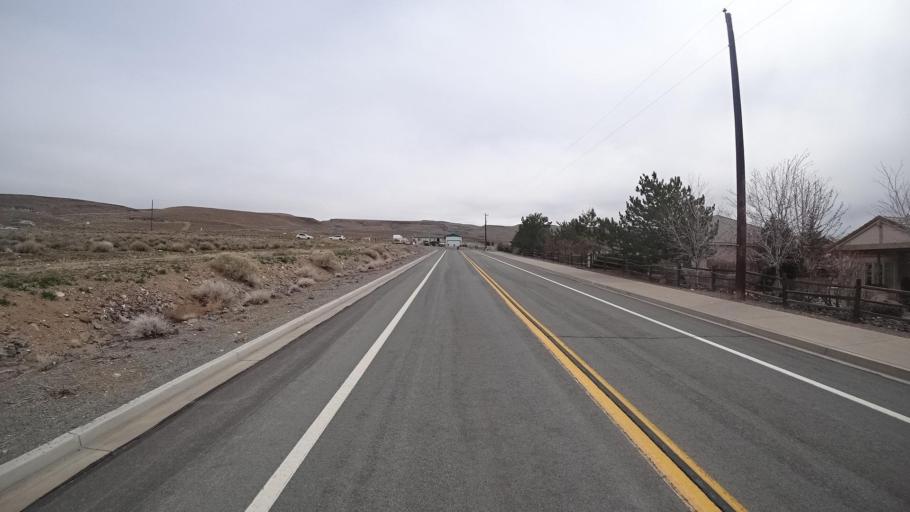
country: US
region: Nevada
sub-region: Washoe County
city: Spanish Springs
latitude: 39.6363
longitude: -119.6647
